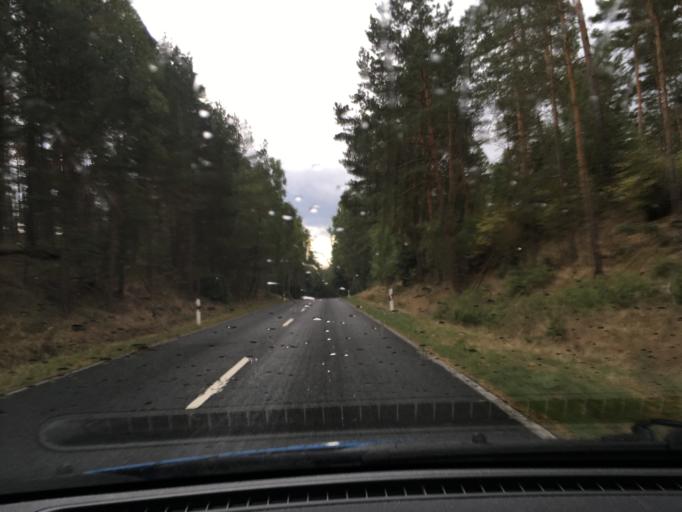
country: DE
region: Lower Saxony
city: Wietzendorf
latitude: 52.8943
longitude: 10.0059
